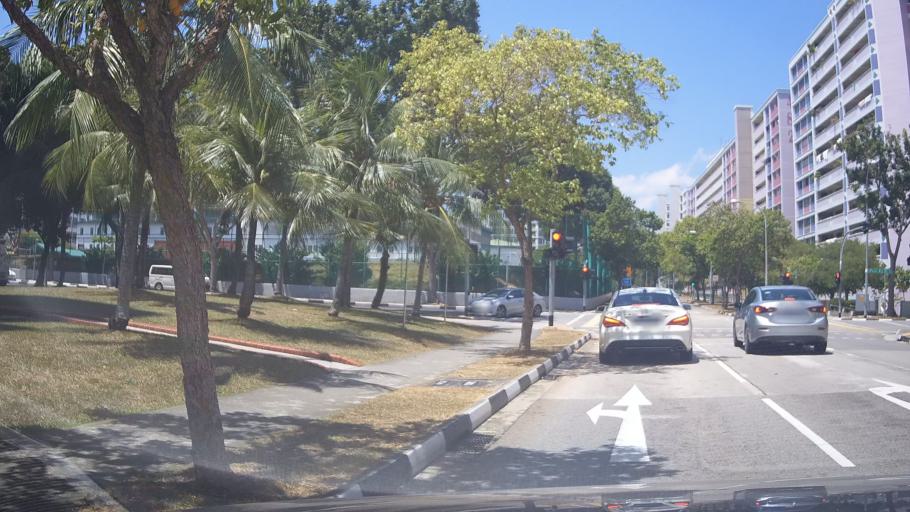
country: MY
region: Johor
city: Kampung Pasir Gudang Baru
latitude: 1.3730
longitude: 103.9614
